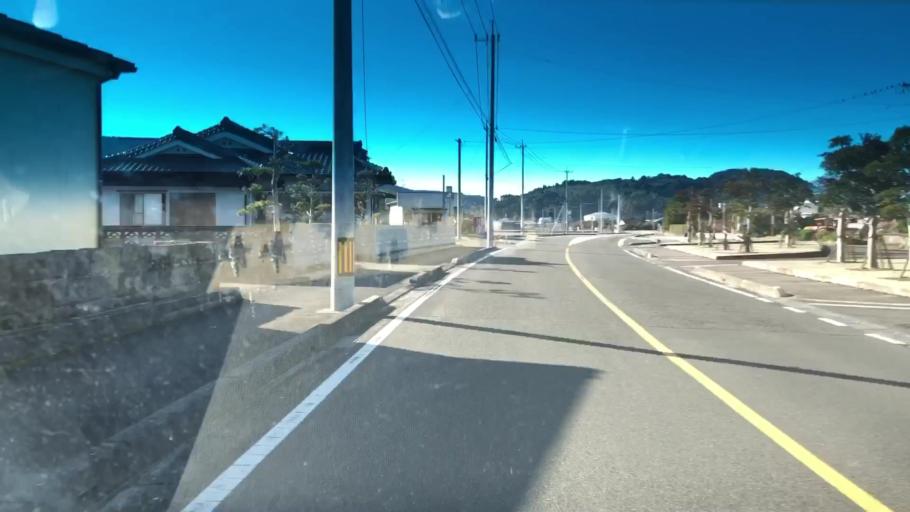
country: JP
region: Kagoshima
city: Satsumasendai
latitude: 31.8166
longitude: 130.2843
